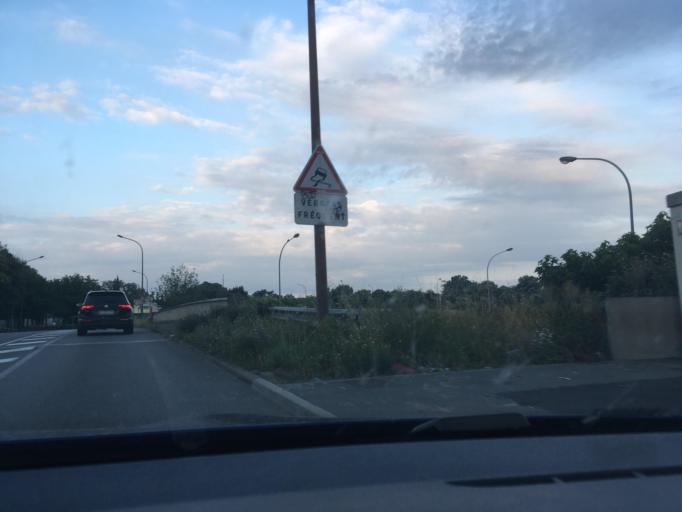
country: FR
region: Midi-Pyrenees
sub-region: Departement de la Haute-Garonne
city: Blagnac
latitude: 43.6059
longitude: 1.3957
